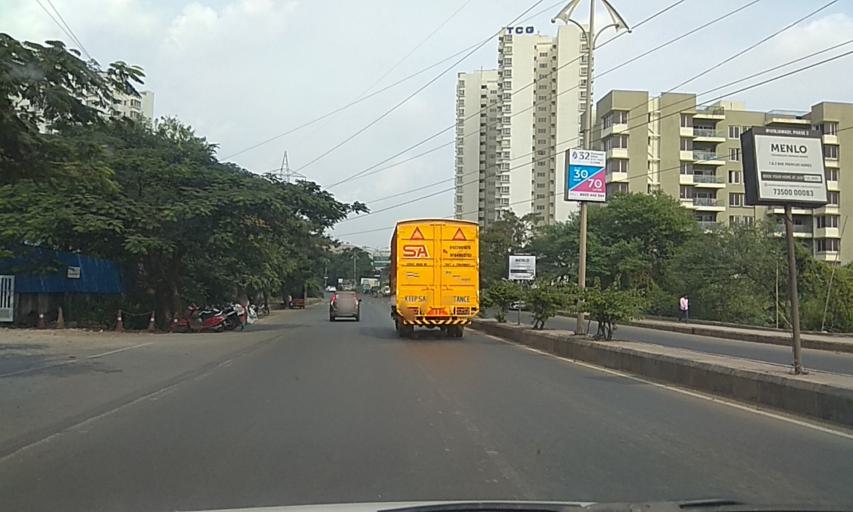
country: IN
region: Maharashtra
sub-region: Pune Division
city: Pimpri
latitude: 18.5904
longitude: 73.7063
